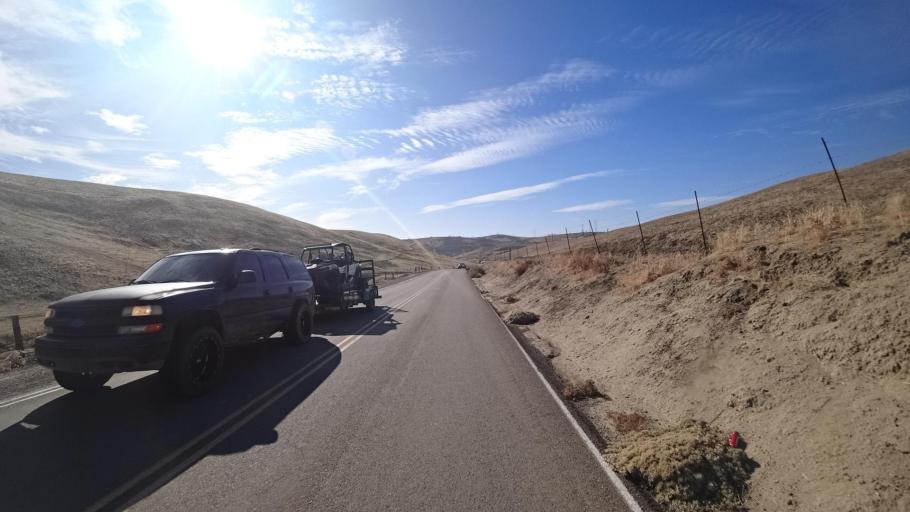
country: US
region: California
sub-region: Kern County
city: Oildale
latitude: 35.5940
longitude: -118.9530
